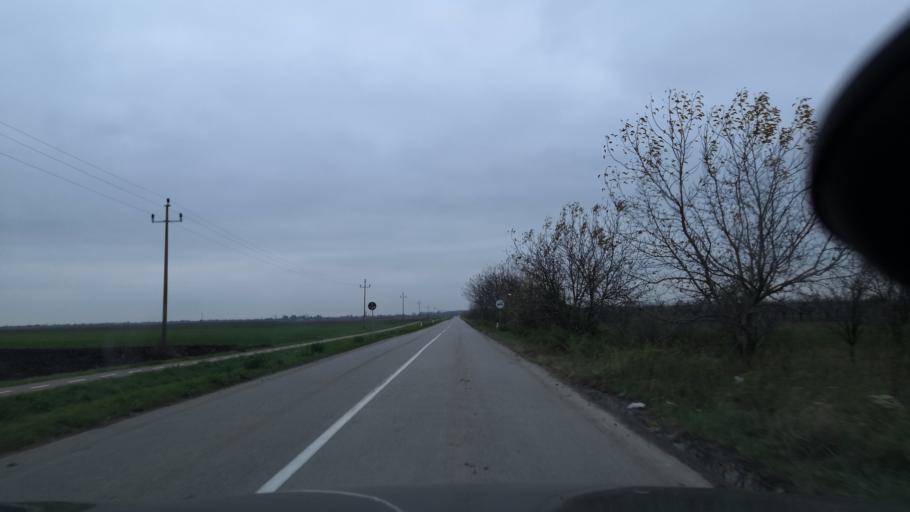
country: HU
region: Csongrad
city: Roszke
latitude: 46.1499
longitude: 20.1033
